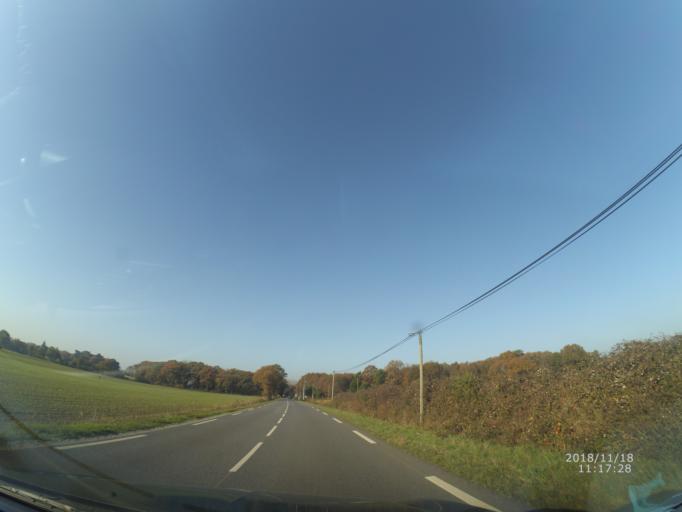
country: FR
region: Pays de la Loire
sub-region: Departement de la Loire-Atlantique
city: Saint-Pere-en-Retz
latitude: 47.2189
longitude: -2.0629
